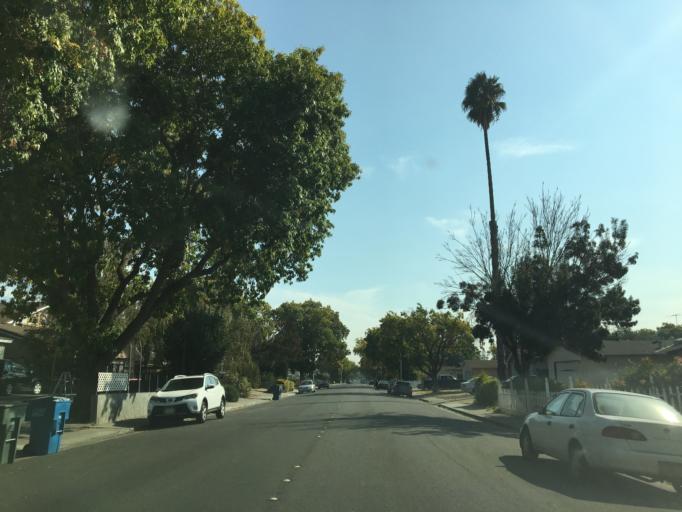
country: US
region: California
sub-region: Santa Clara County
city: Milpitas
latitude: 37.4357
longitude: -121.8754
